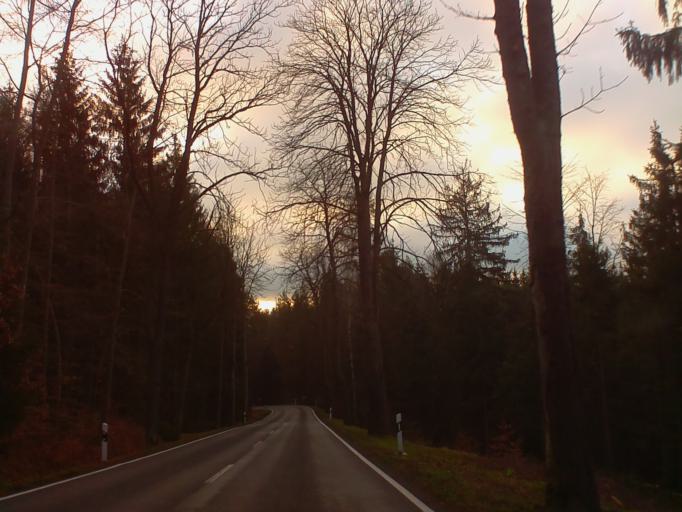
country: DE
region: Thuringia
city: Neustadt (Orla)
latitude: 50.7521
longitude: 11.7167
